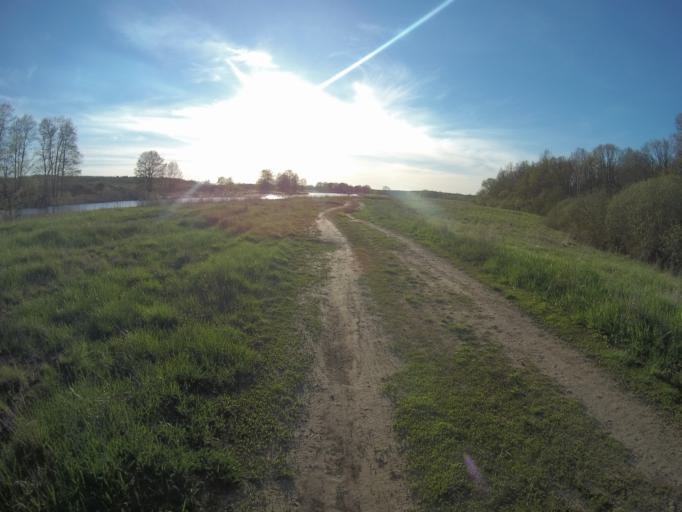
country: RU
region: Vladimir
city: Raduzhnyy
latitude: 56.0300
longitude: 40.2842
